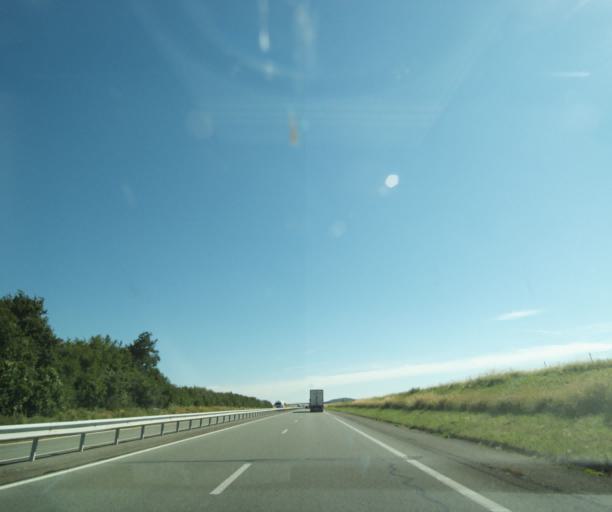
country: FR
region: Champagne-Ardenne
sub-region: Departement de la Haute-Marne
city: Avrecourt
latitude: 48.0307
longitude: 5.5480
